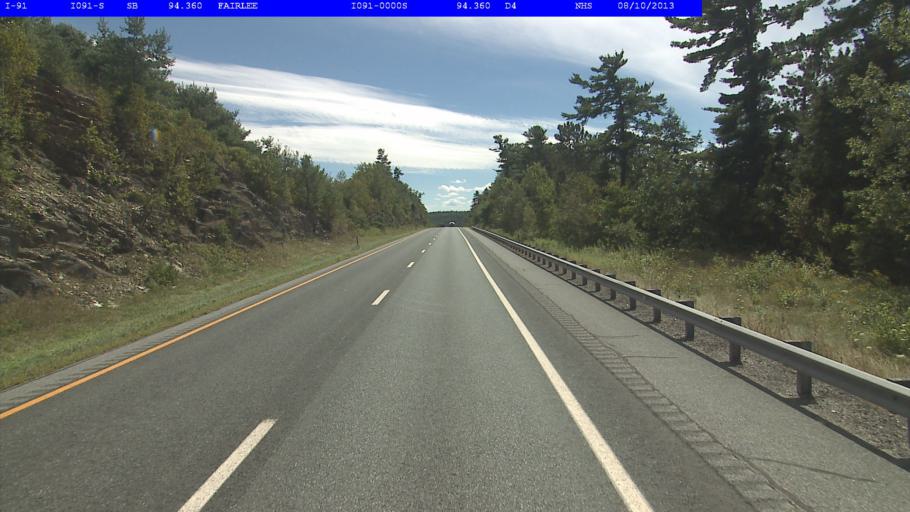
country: US
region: New Hampshire
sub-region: Grafton County
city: Orford
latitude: 43.9385
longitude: -72.1334
